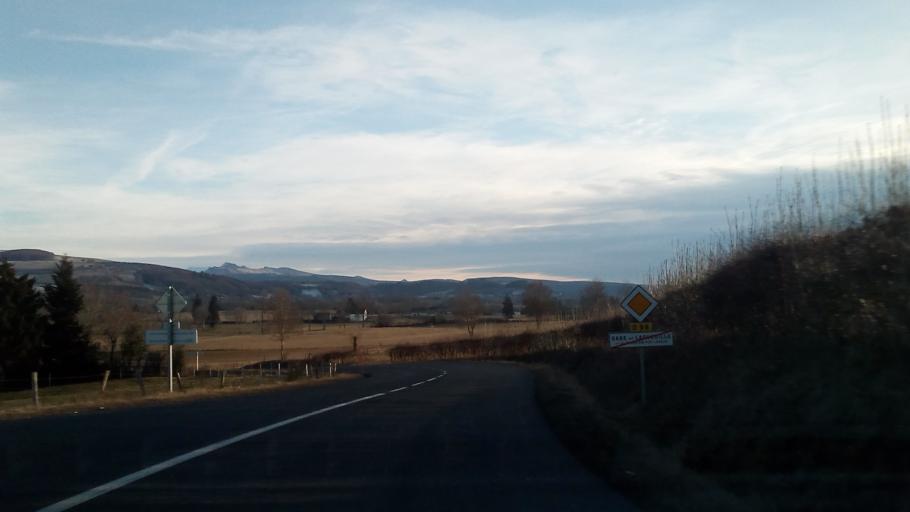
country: FR
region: Auvergne
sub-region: Departement du Puy-de-Dome
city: Saint-Sauves-d'Auvergne
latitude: 45.6485
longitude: 2.7084
